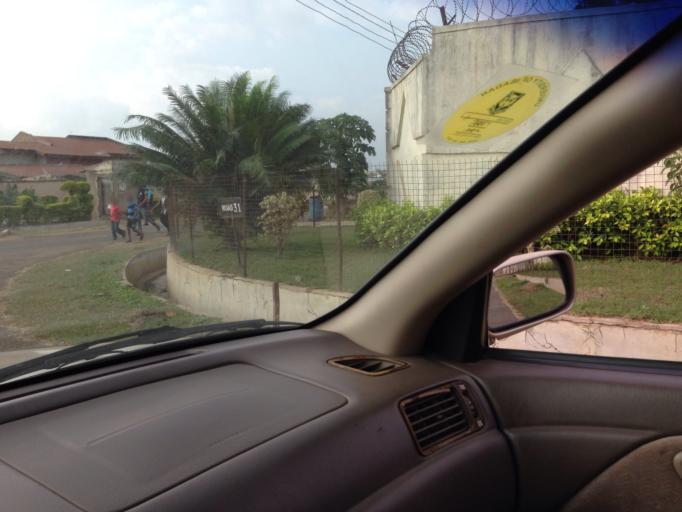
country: NG
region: Oyo
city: Ibadan
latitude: 7.4281
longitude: 3.9455
